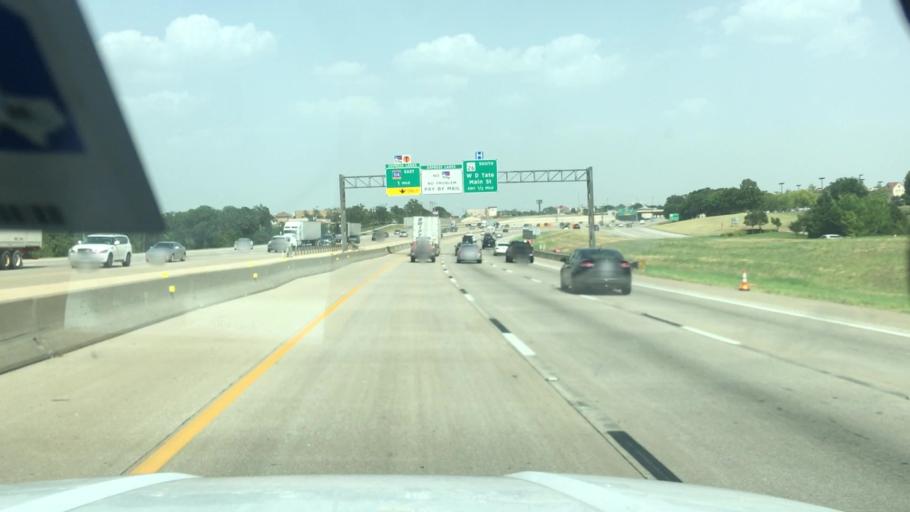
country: US
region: Texas
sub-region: Tarrant County
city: Southlake
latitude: 32.9429
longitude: -97.1084
